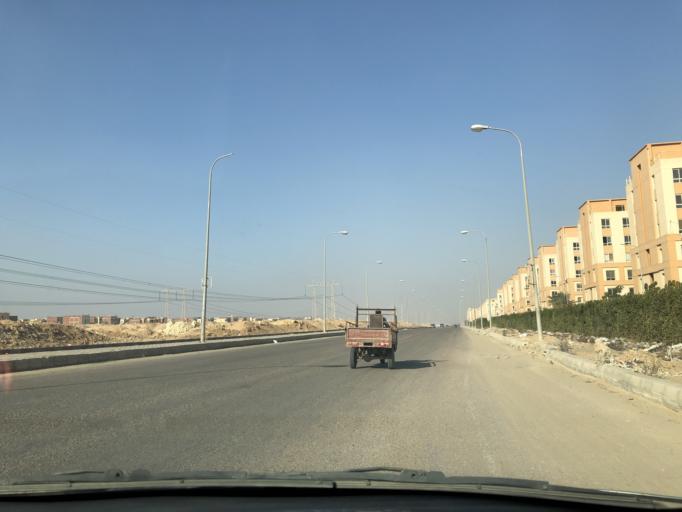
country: EG
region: Al Jizah
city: Madinat Sittah Uktubar
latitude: 29.9078
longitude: 31.0513
